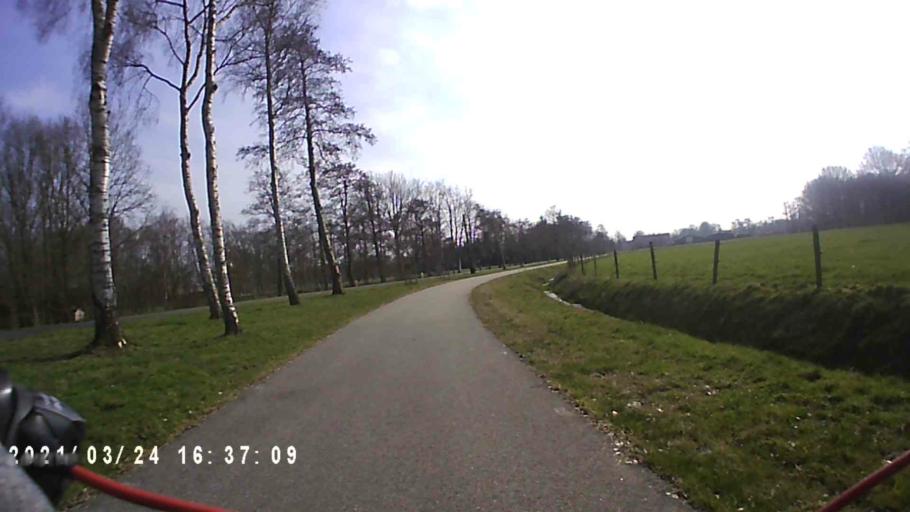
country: NL
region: Groningen
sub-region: Gemeente Leek
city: Leek
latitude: 53.0627
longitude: 6.2820
